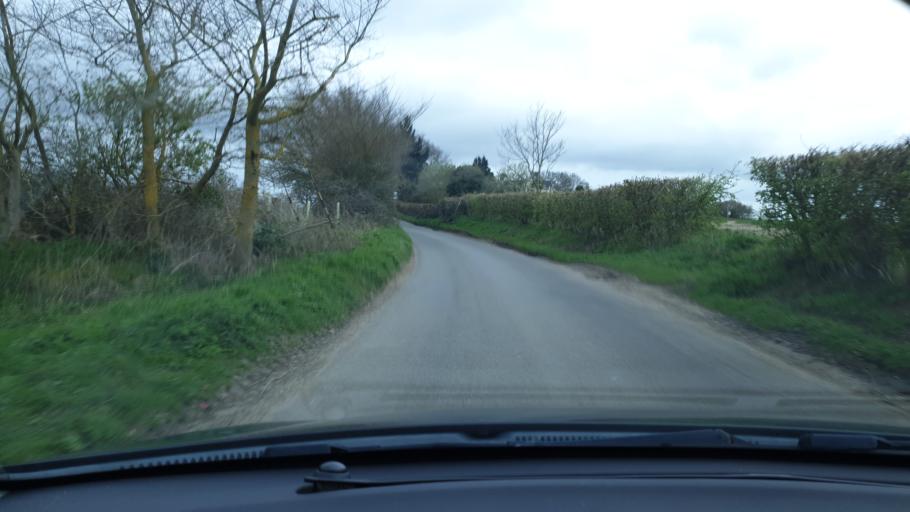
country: GB
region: England
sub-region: Suffolk
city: Shotley Gate
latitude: 51.9280
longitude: 1.1782
